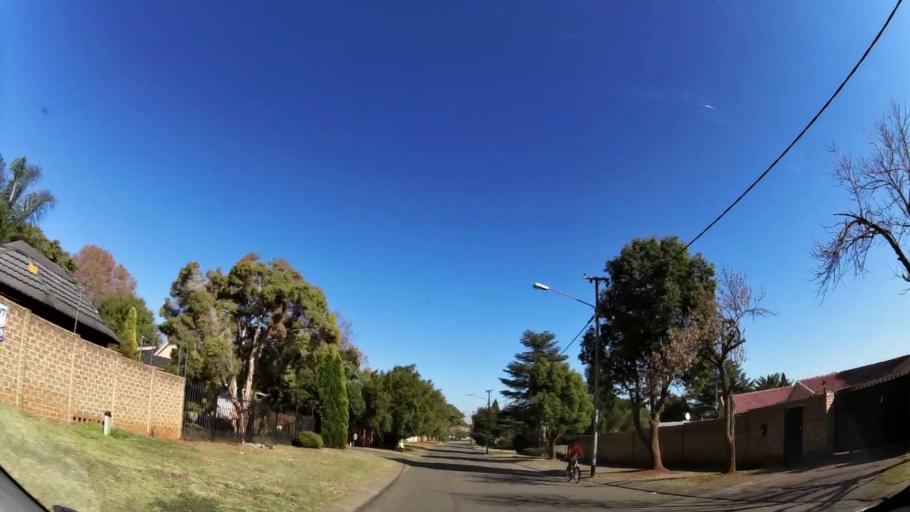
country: ZA
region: Gauteng
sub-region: City of Tshwane Metropolitan Municipality
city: Centurion
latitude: -25.8597
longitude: 28.2105
